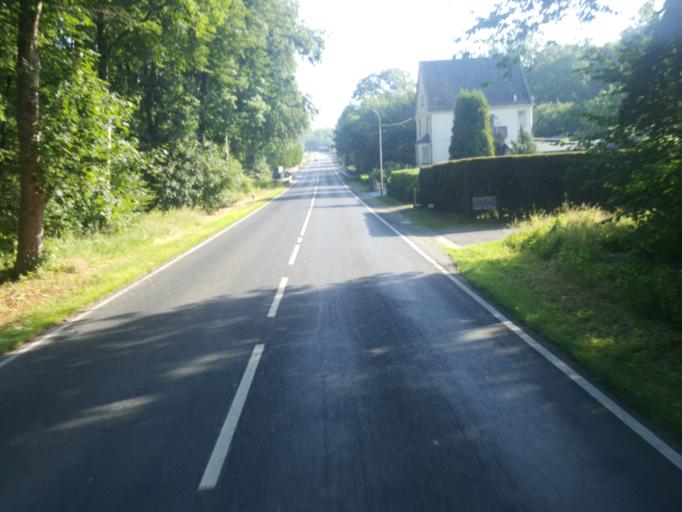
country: DE
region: Rheinland-Pfalz
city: Dreikirchen
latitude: 50.4459
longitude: 7.9412
